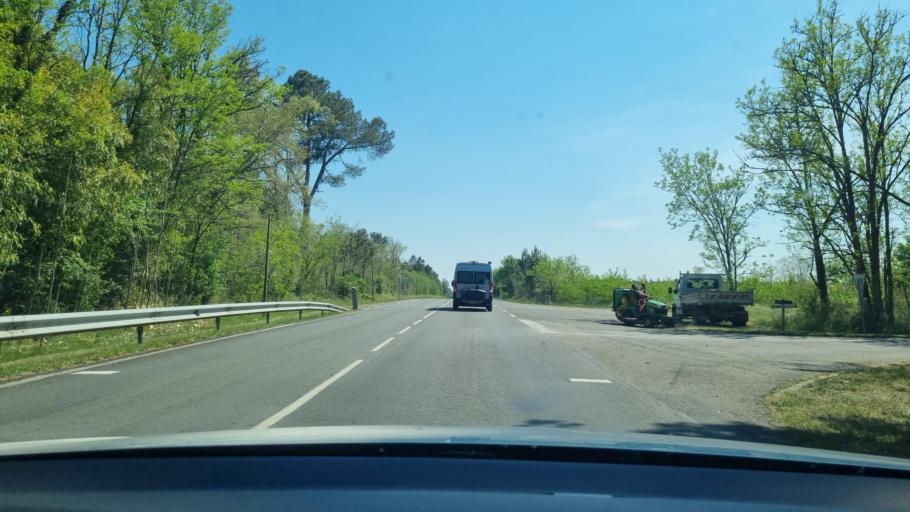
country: FR
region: Aquitaine
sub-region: Departement de la Gironde
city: Prechac
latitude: 44.2827
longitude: -0.2619
